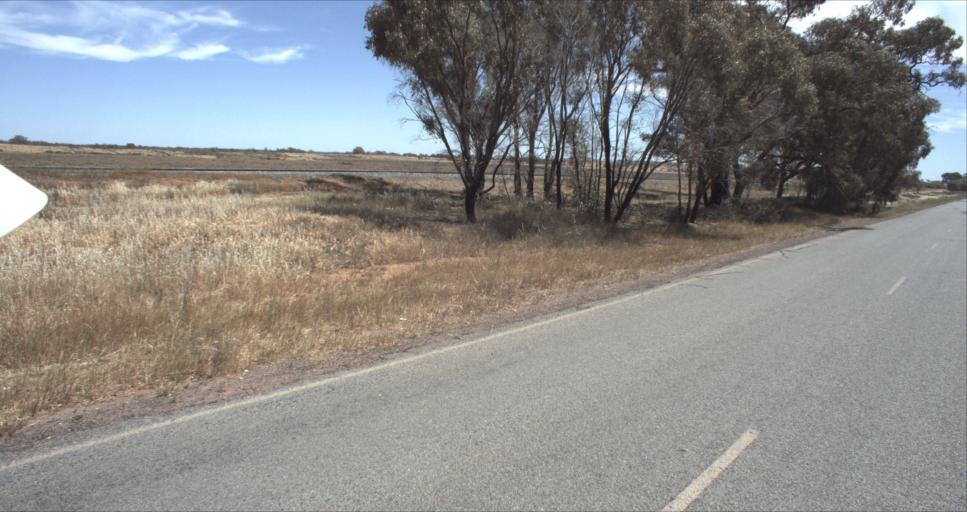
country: AU
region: New South Wales
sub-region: Leeton
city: Leeton
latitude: -34.6424
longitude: 146.4680
